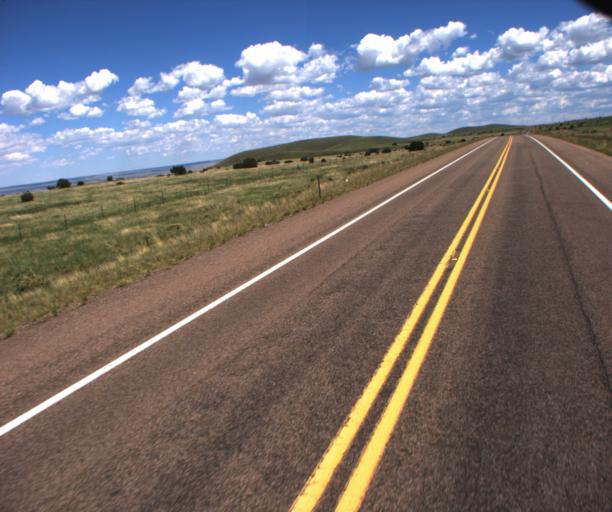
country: US
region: Arizona
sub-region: Apache County
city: Springerville
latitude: 34.2448
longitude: -109.5239
